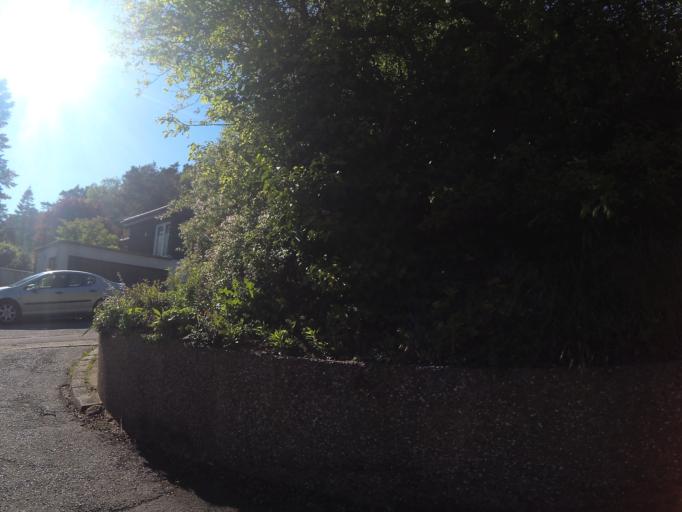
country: DE
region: Saarland
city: Britten
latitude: 49.4783
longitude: 6.6739
